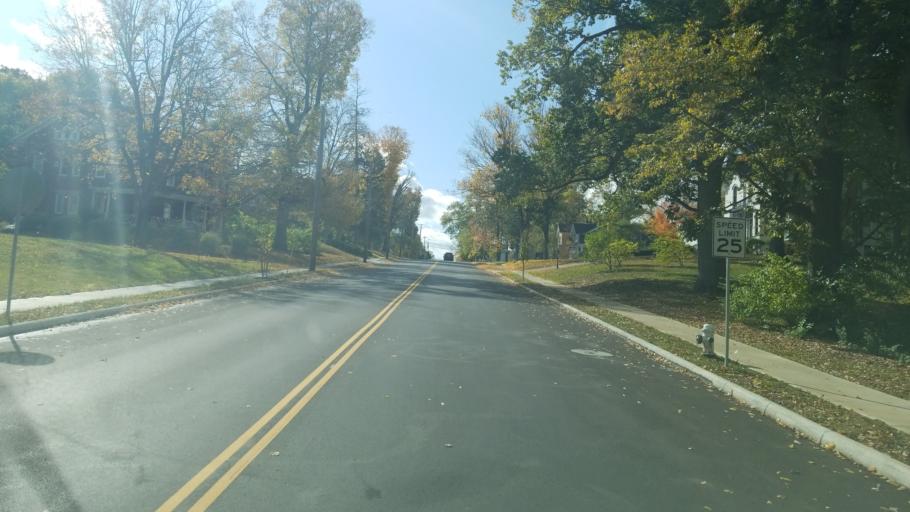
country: US
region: Ohio
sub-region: Warren County
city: Lebanon
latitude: 39.4310
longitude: -84.2087
